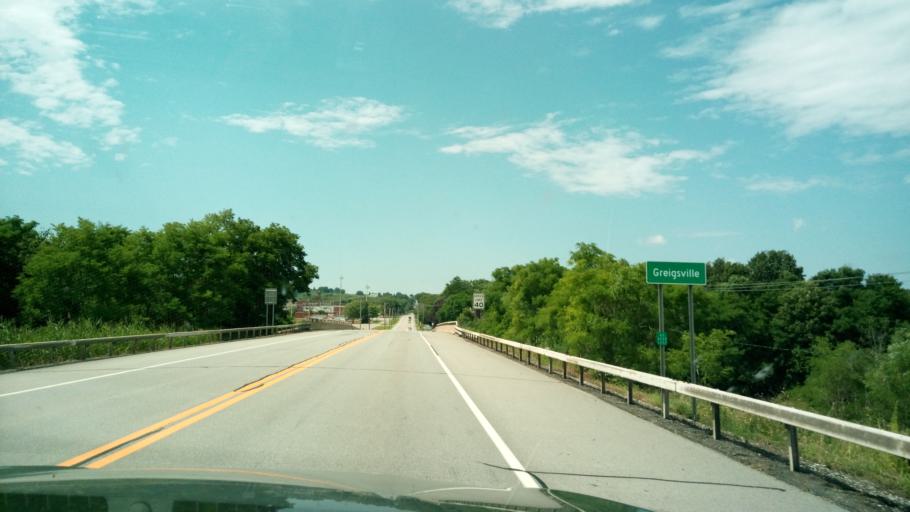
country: US
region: New York
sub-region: Livingston County
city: Geneseo
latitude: 42.8307
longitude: -77.8862
